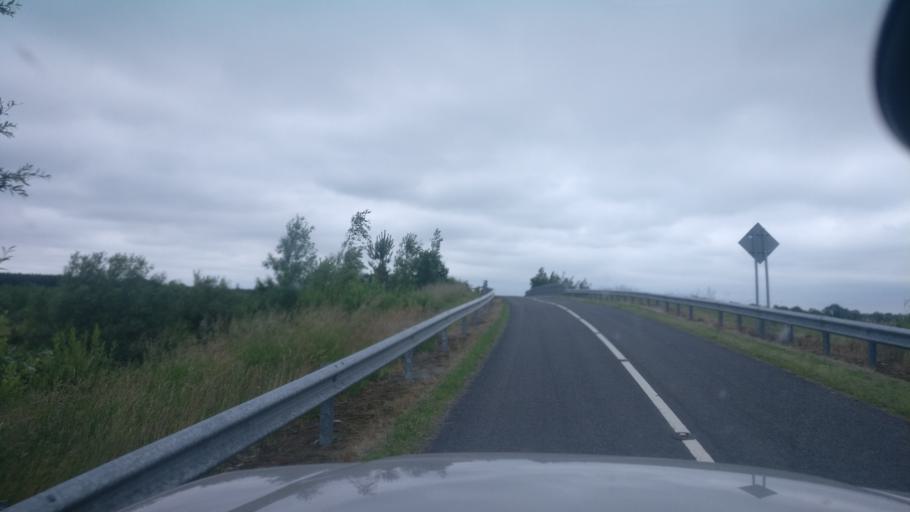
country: IE
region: Connaught
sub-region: County Galway
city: Ballinasloe
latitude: 53.2900
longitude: -8.3756
